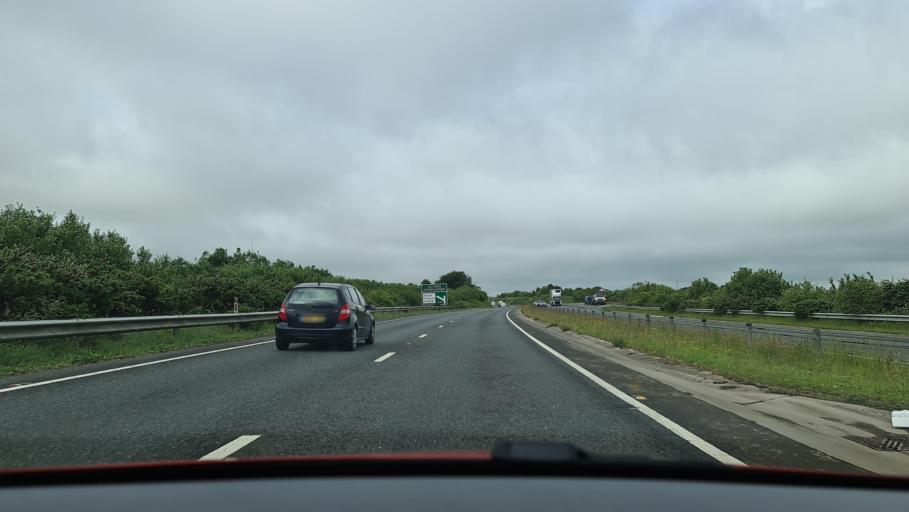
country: GB
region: England
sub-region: Cornwall
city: Bugle
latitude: 50.4297
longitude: -4.7988
